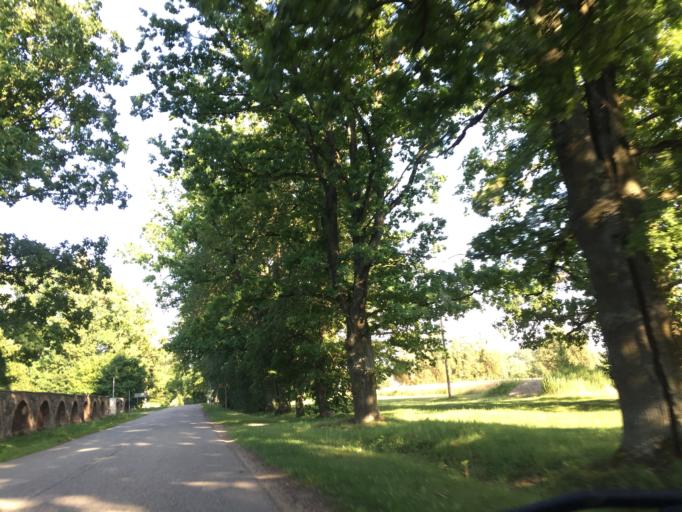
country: LT
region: Siauliu apskritis
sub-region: Joniskis
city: Joniskis
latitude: 56.4228
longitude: 23.6978
